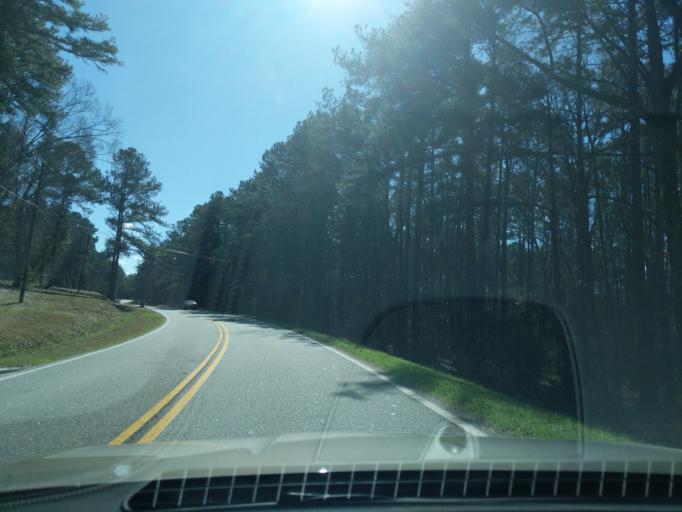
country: US
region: Georgia
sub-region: Columbia County
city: Evans
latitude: 33.5448
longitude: -82.1658
